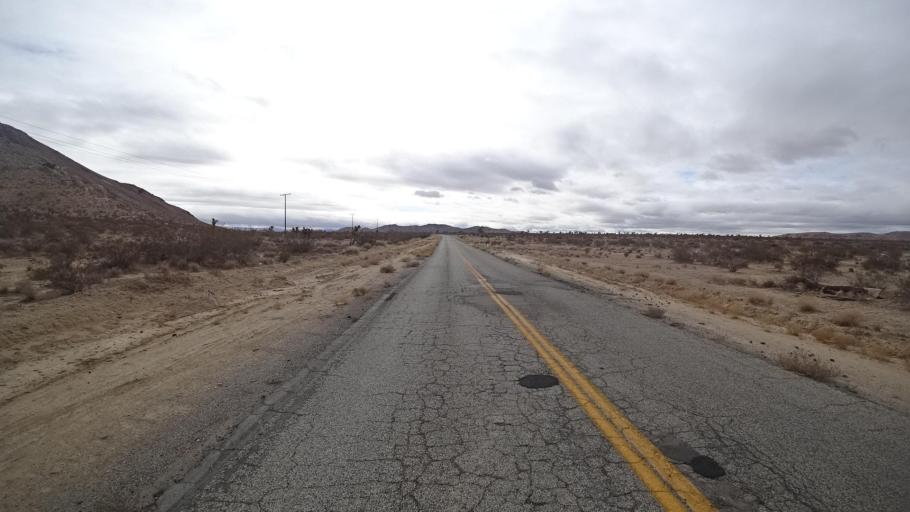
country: US
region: California
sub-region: Kern County
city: Mojave
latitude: 34.9689
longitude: -118.2112
